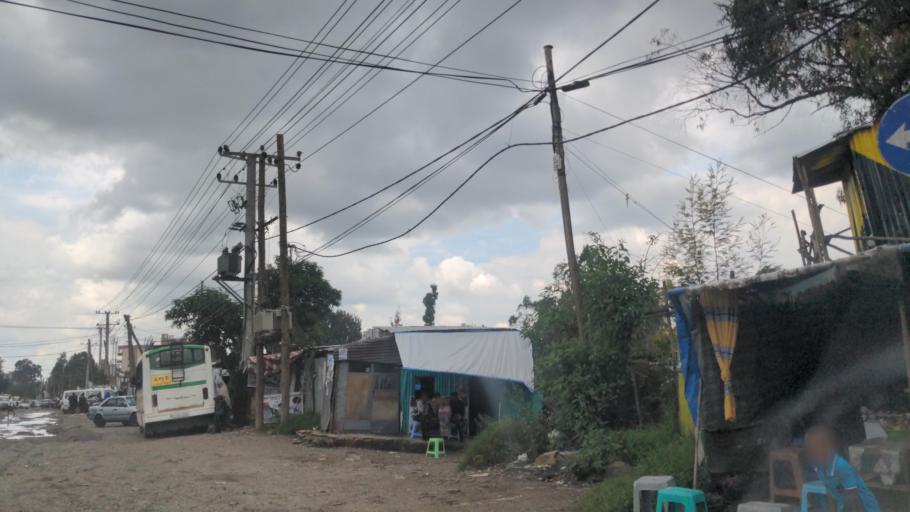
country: ET
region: Adis Abeba
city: Addis Ababa
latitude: 9.0151
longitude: 38.7907
